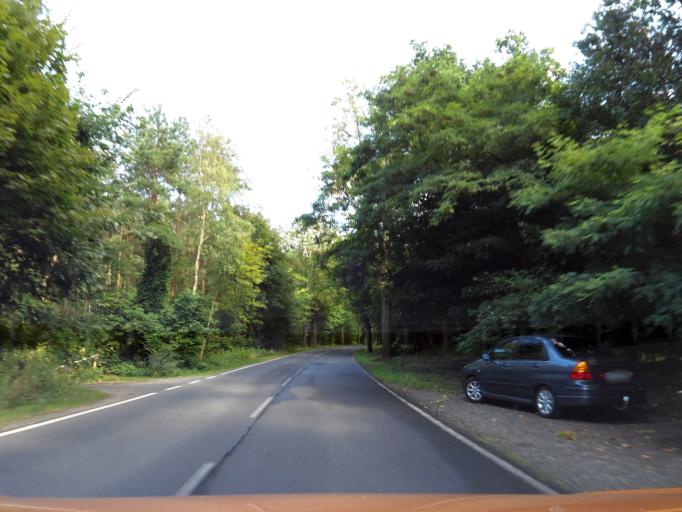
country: DE
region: Berlin
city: Staaken
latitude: 52.5094
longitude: 13.1356
